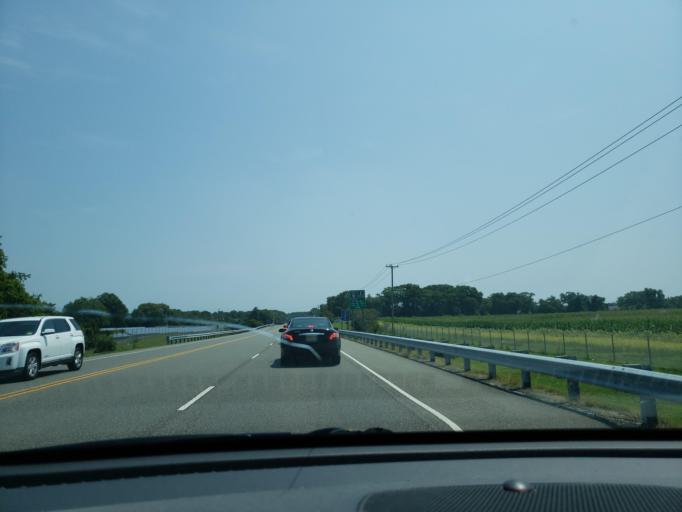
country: US
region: New Jersey
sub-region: Cape May County
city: Erma
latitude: 38.9704
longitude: -74.9252
